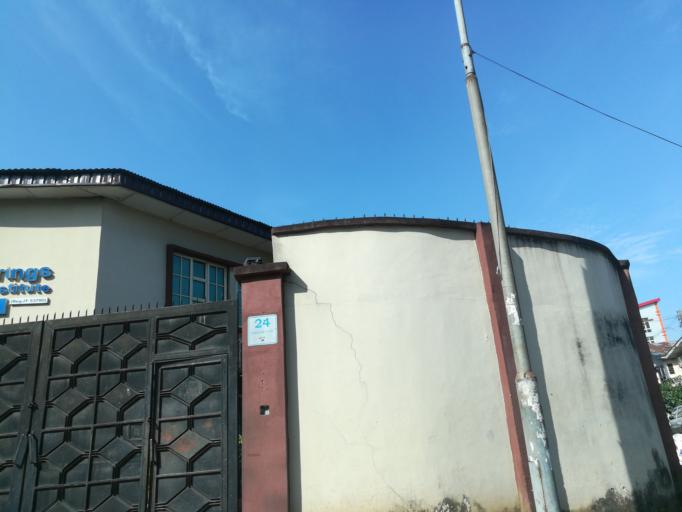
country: NG
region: Lagos
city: Ikeja
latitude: 6.5996
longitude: 3.3412
